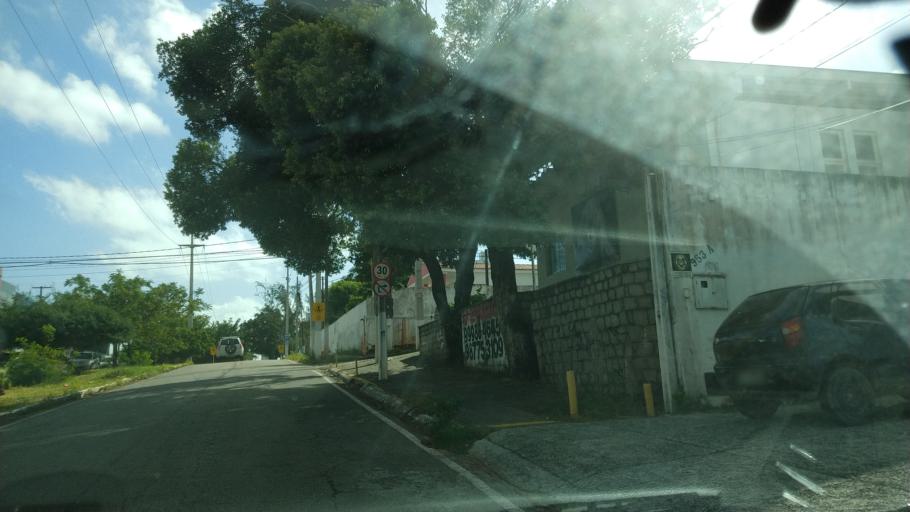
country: BR
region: Rio Grande do Norte
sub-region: Natal
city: Natal
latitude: -5.8021
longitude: -35.2044
